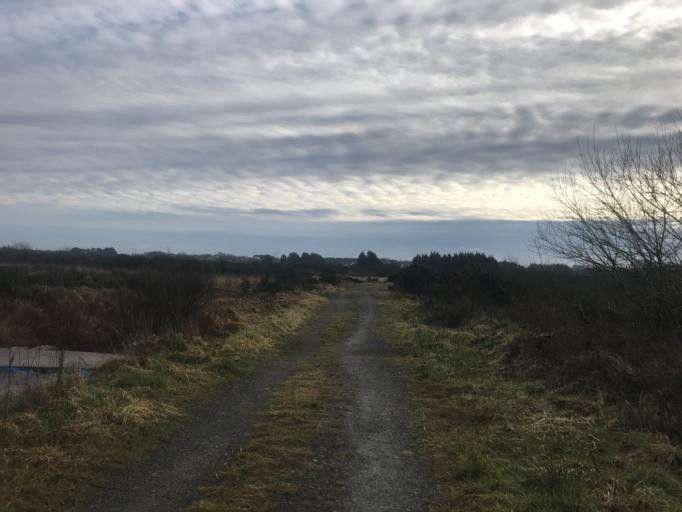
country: IE
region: Connaught
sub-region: County Galway
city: Claregalway
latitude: 53.3207
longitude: -9.0061
